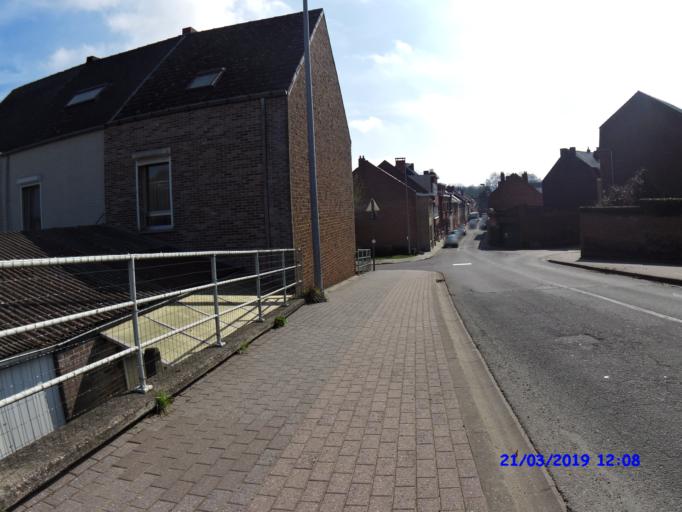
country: BE
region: Flanders
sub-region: Provincie Vlaams-Brabant
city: Halle
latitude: 50.7160
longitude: 4.2229
